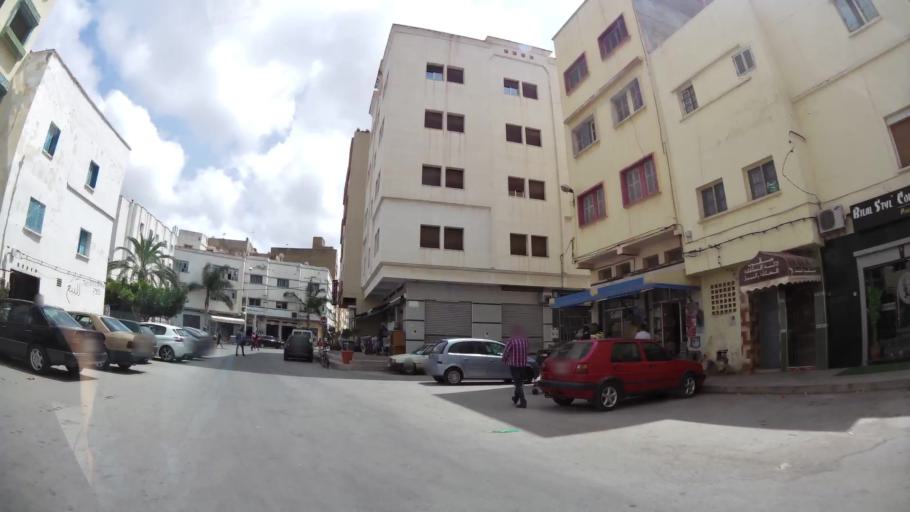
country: MA
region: Oriental
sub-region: Nador
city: Nador
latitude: 35.1729
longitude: -2.9268
